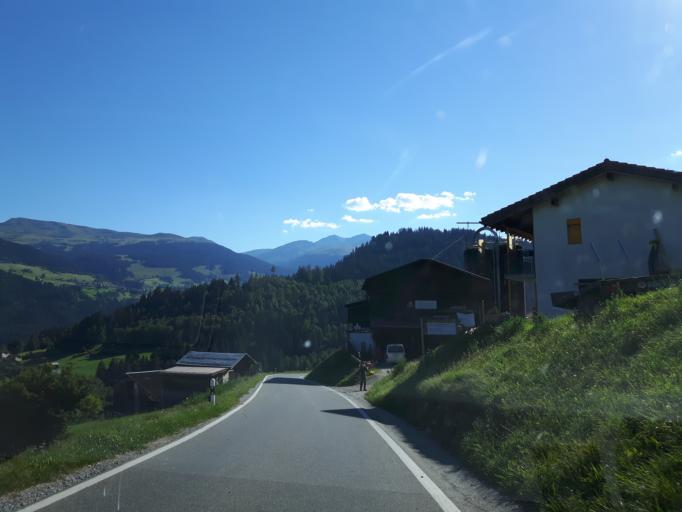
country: CH
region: Grisons
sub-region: Surselva District
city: Breil
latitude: 46.7804
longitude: 9.1066
